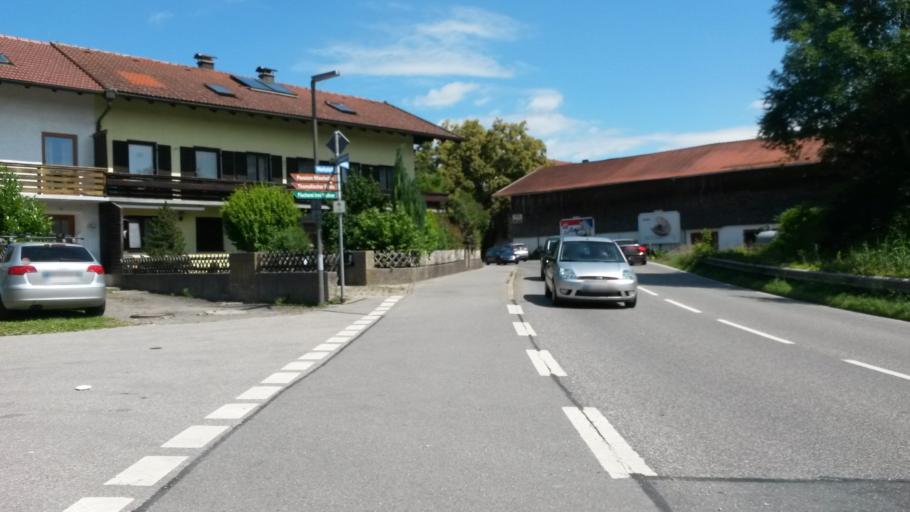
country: DE
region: Bavaria
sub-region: Upper Bavaria
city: Chieming
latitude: 47.8889
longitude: 12.5343
